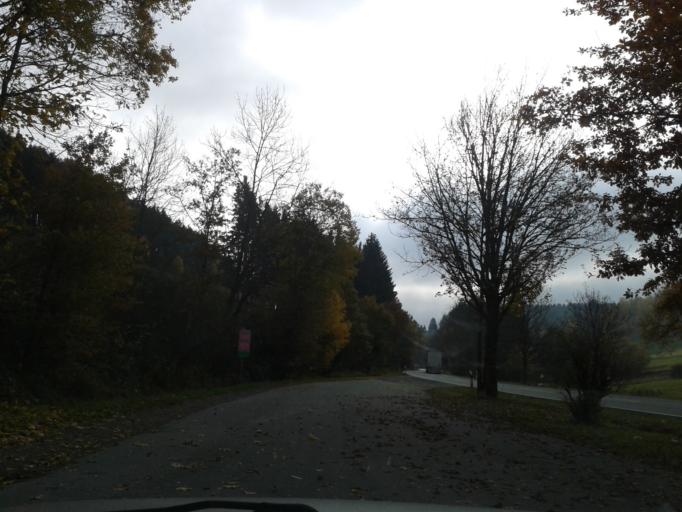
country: DE
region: North Rhine-Westphalia
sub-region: Regierungsbezirk Arnsberg
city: Bad Berleburg
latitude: 51.0091
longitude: 8.3689
